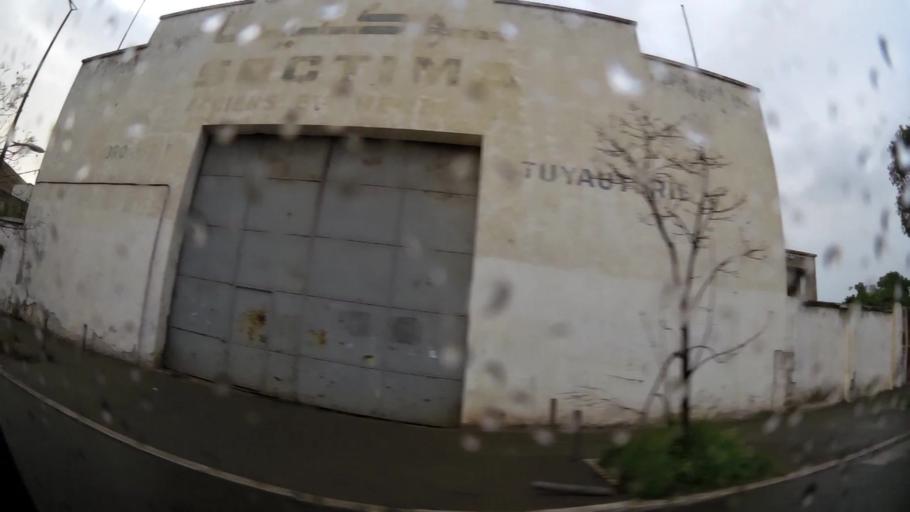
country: MA
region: Grand Casablanca
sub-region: Casablanca
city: Casablanca
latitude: 33.5776
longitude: -7.5517
